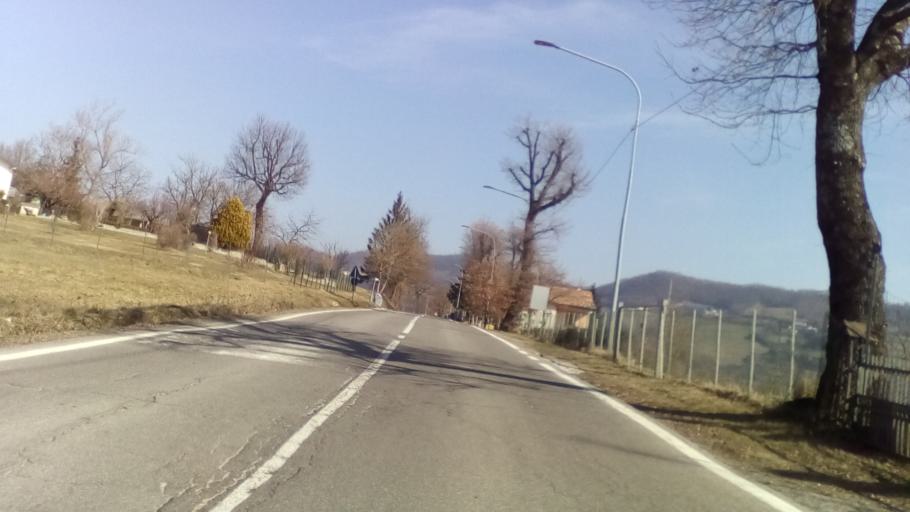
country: IT
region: Emilia-Romagna
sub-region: Provincia di Modena
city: Pavullo nel Frignano
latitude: 44.3123
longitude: 10.7947
